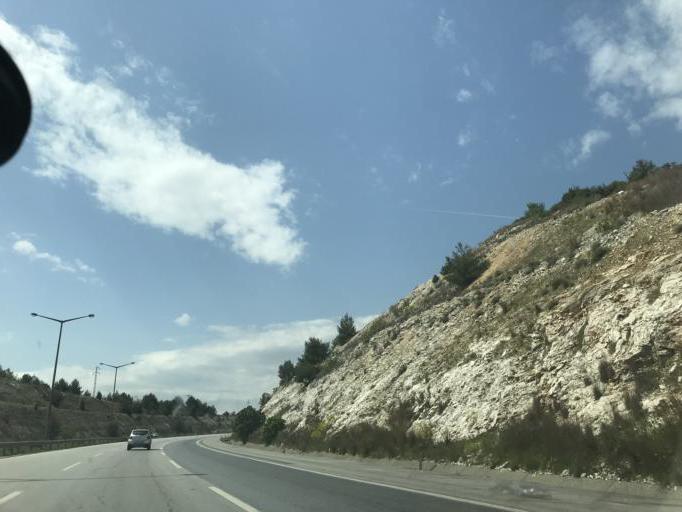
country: TR
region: Mersin
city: Tarsus
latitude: 37.1369
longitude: 34.8467
